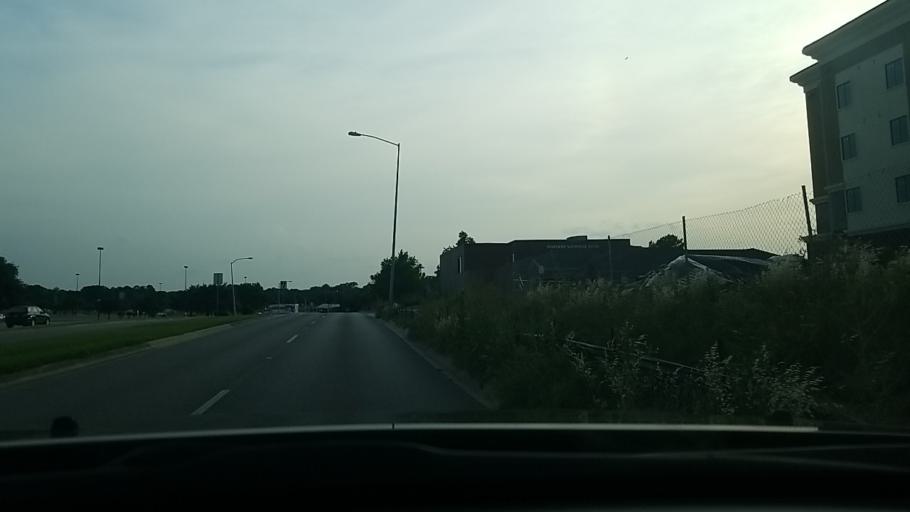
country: US
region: Texas
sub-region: Denton County
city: Denton
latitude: 33.1929
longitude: -97.1081
